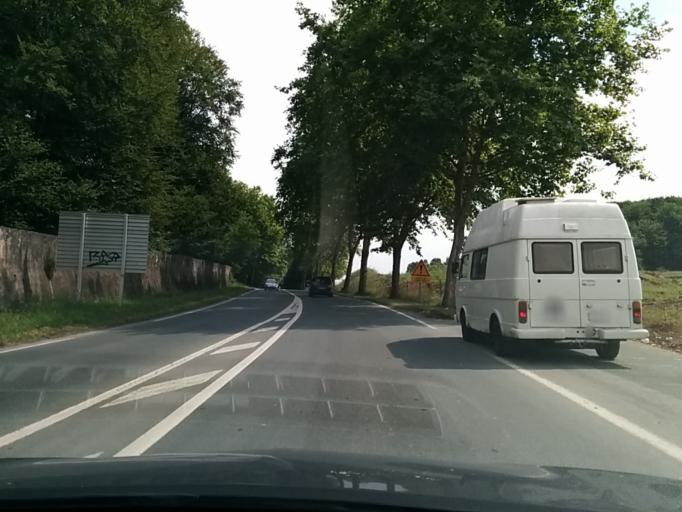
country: FR
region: Aquitaine
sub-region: Departement des Pyrenees-Atlantiques
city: Urrugne
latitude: 43.3640
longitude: -1.6906
